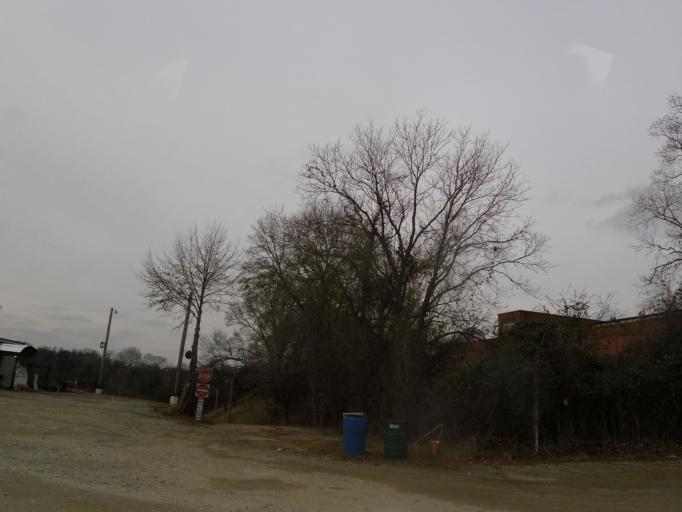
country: US
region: Alabama
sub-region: Montgomery County
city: Montgomery
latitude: 32.3926
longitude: -86.3160
